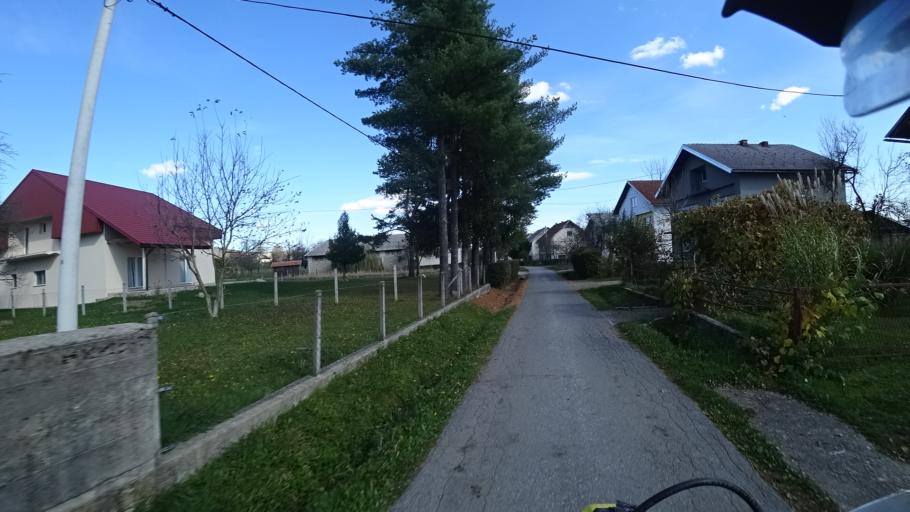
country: HR
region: Karlovacka
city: Plaski
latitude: 45.0874
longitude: 15.3618
